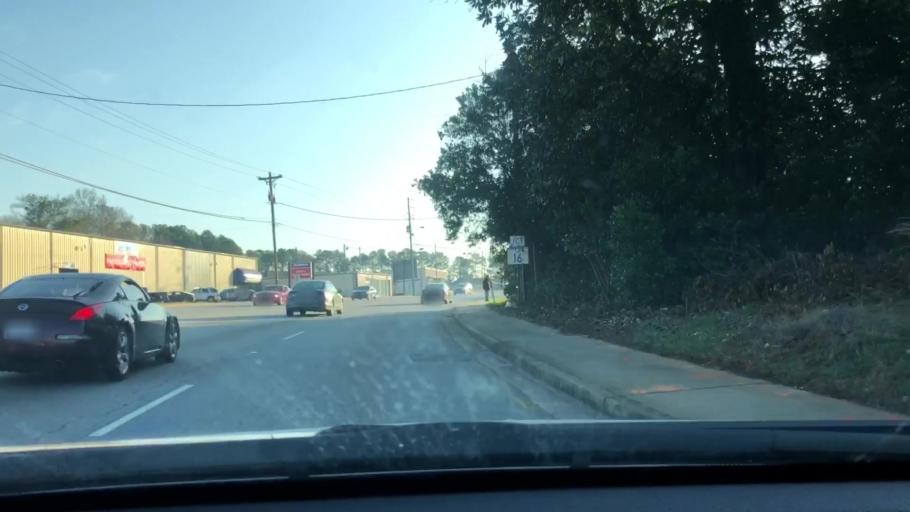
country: US
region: South Carolina
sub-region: Richland County
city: Columbia
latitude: 34.0289
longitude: -81.0574
